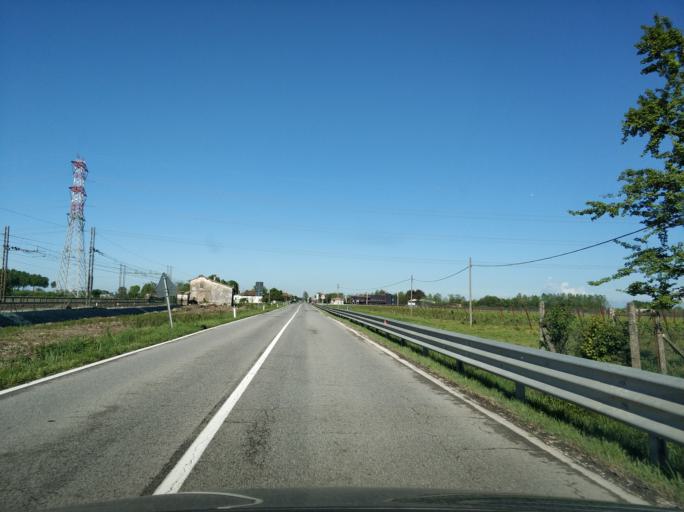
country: IT
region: Friuli Venezia Giulia
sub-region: Provincia di Udine
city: Torviscosa
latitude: 45.8280
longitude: 13.2475
